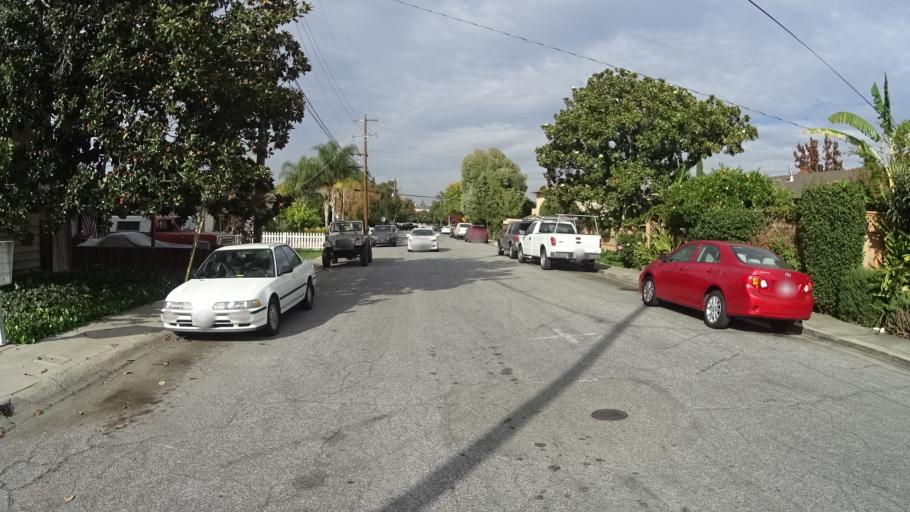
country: US
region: California
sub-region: Santa Clara County
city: Burbank
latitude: 37.3243
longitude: -121.9349
